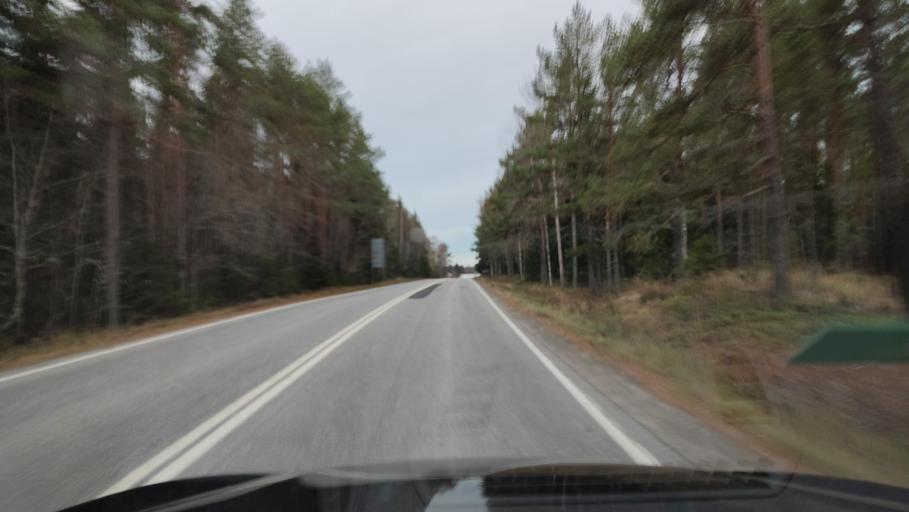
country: FI
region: Ostrobothnia
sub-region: Sydosterbotten
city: Naerpes
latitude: 62.4014
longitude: 21.3599
